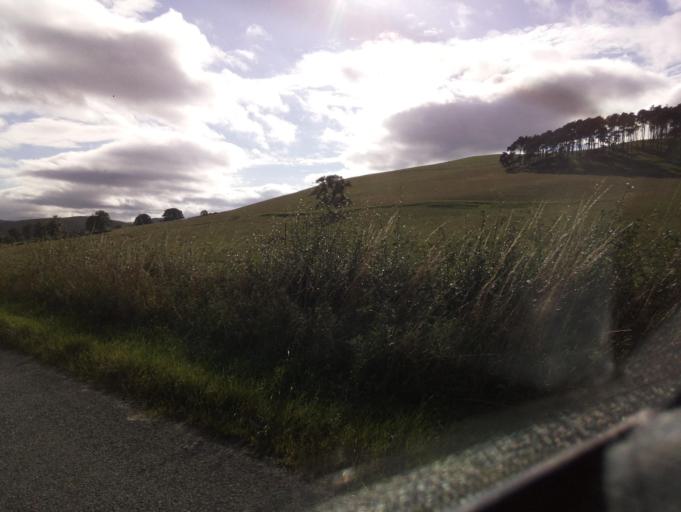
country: GB
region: Scotland
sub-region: South Lanarkshire
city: Biggar
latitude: 55.6231
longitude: -3.4148
